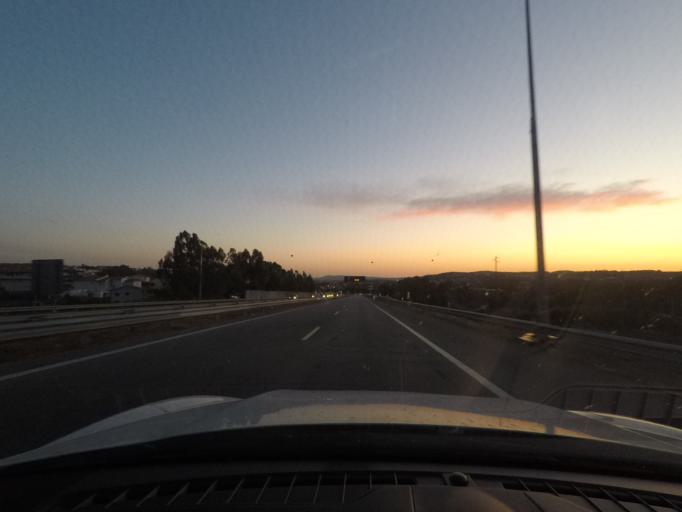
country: PT
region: Porto
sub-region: Pacos de Ferreira
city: Frazao
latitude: 41.2619
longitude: -8.3875
